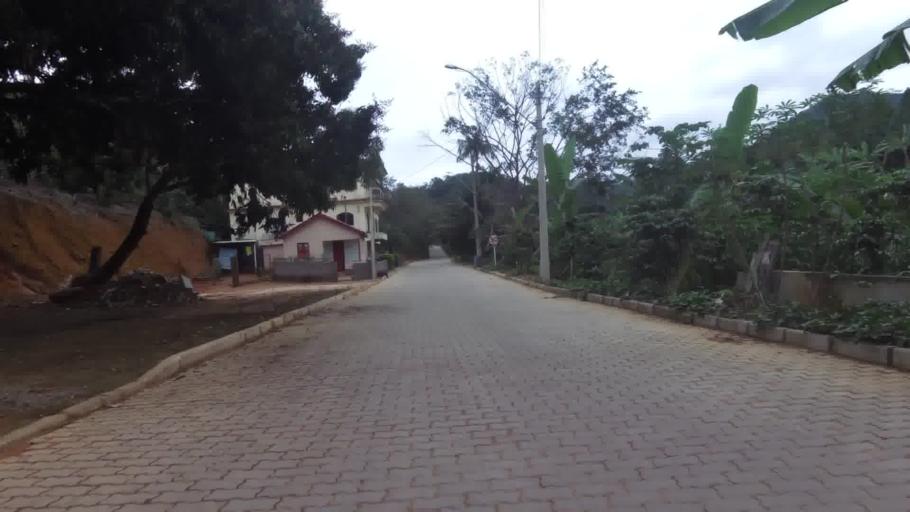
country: BR
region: Espirito Santo
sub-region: Iconha
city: Iconha
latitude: -20.7827
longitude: -40.8261
